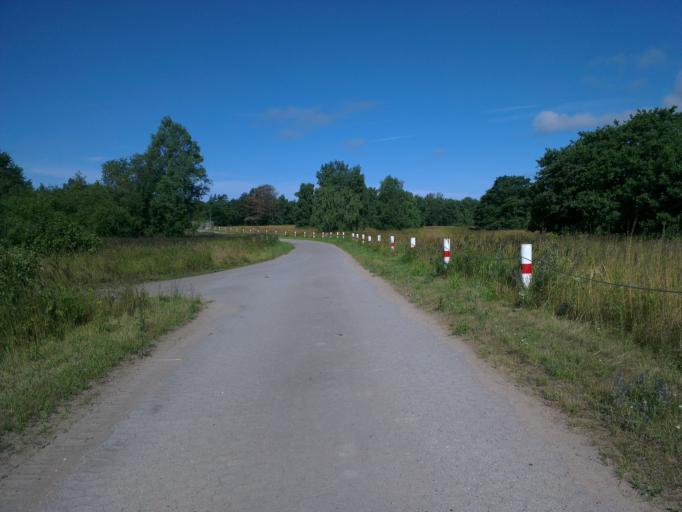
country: DK
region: Capital Region
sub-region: Frederikssund Kommune
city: Jaegerspris
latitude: 55.8931
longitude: 11.9595
